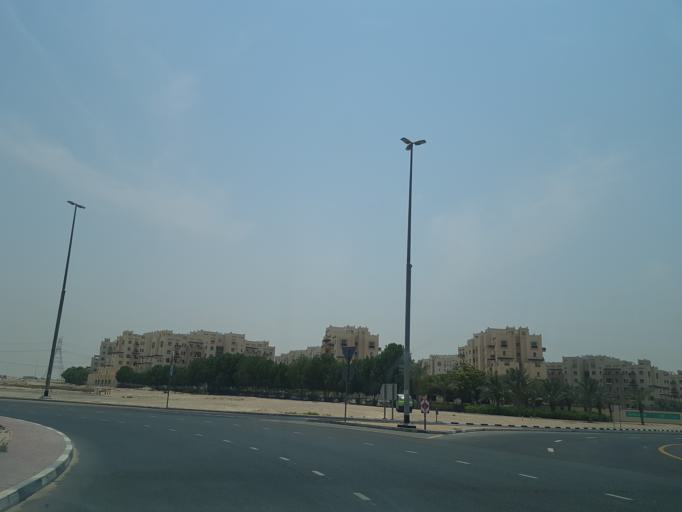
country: AE
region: Dubai
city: Dubai
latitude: 25.0075
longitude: 55.2548
